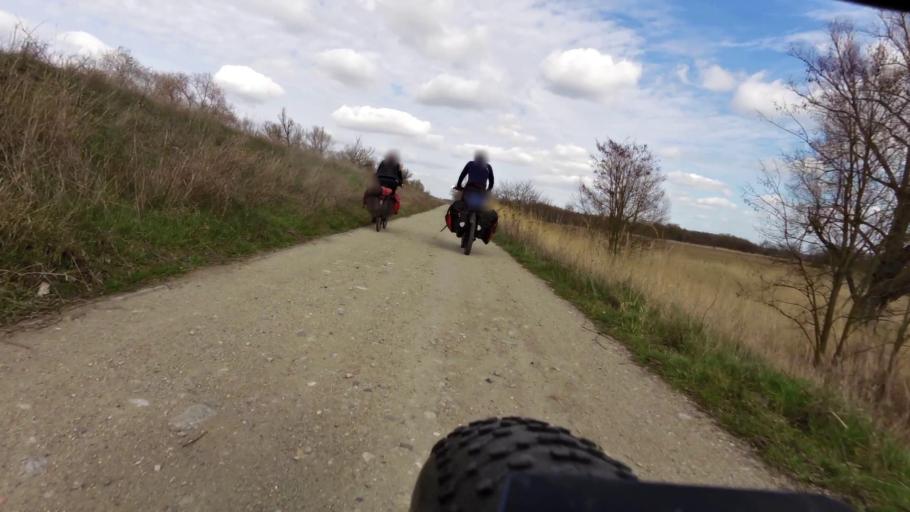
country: DE
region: Brandenburg
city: Lebus
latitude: 52.4331
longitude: 14.5562
